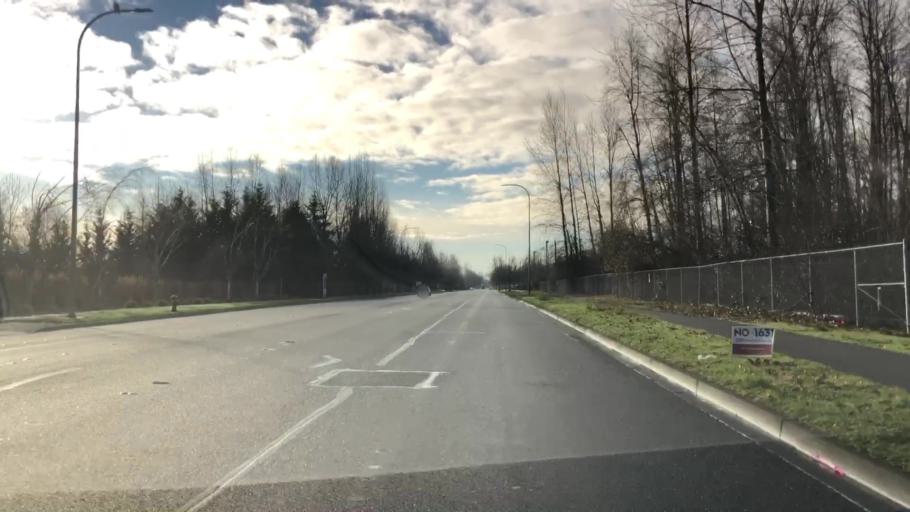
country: US
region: Washington
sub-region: King County
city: Renton
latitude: 47.4518
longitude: -122.2328
